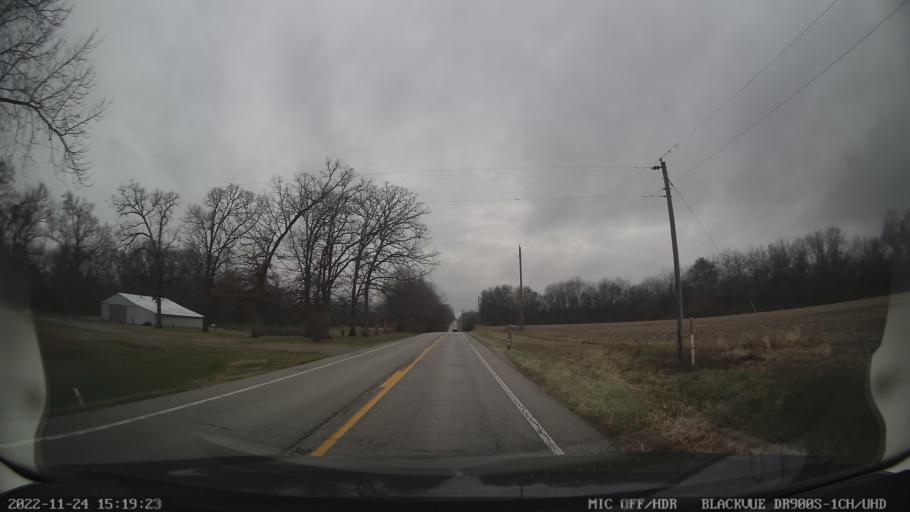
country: US
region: Illinois
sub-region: Macoupin County
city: Staunton
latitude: 38.9685
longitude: -89.7127
